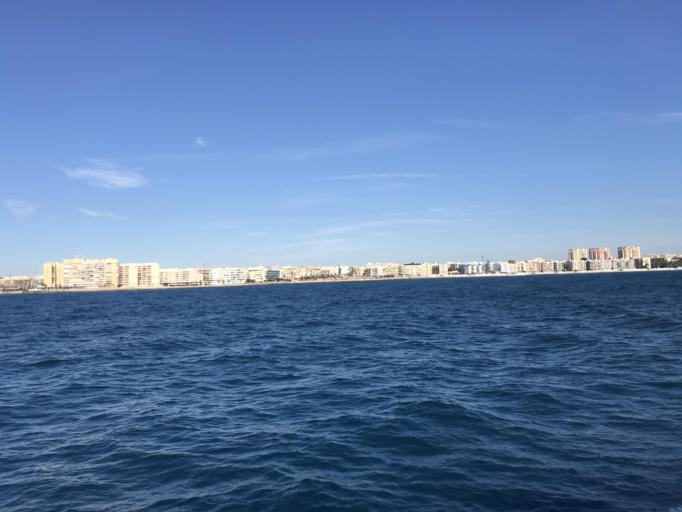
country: ES
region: Valencia
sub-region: Provincia de Alicante
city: Torrevieja
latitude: 37.9725
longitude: -0.6588
